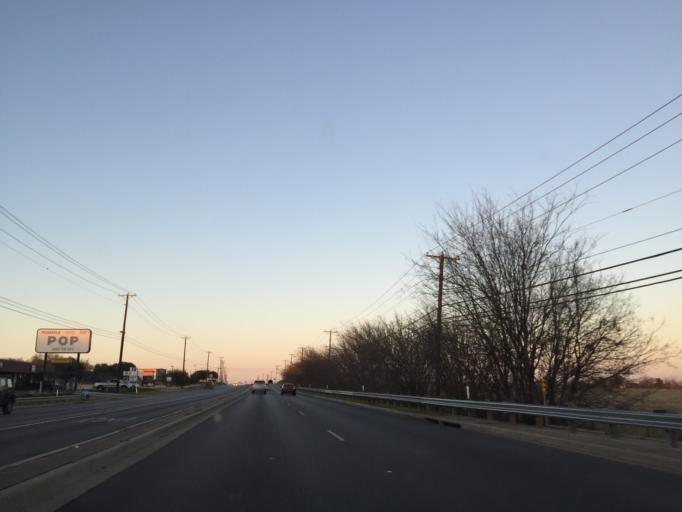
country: US
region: Texas
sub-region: Travis County
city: Pflugerville
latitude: 30.4459
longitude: -97.6079
